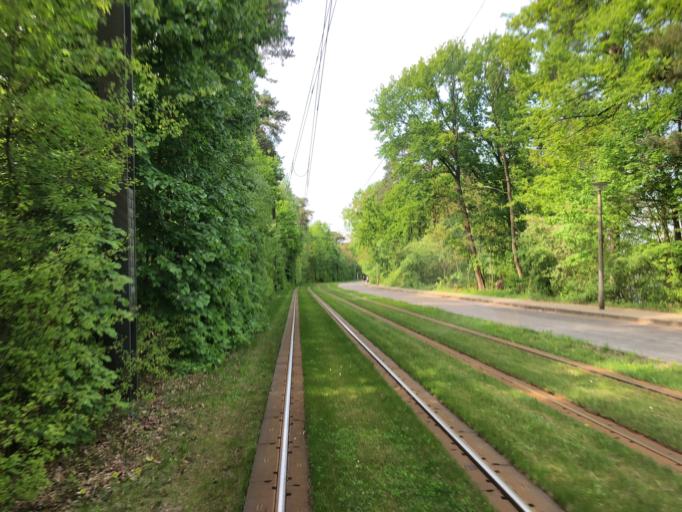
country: DE
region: Berlin
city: Schmockwitz
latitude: 52.3990
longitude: 13.6265
